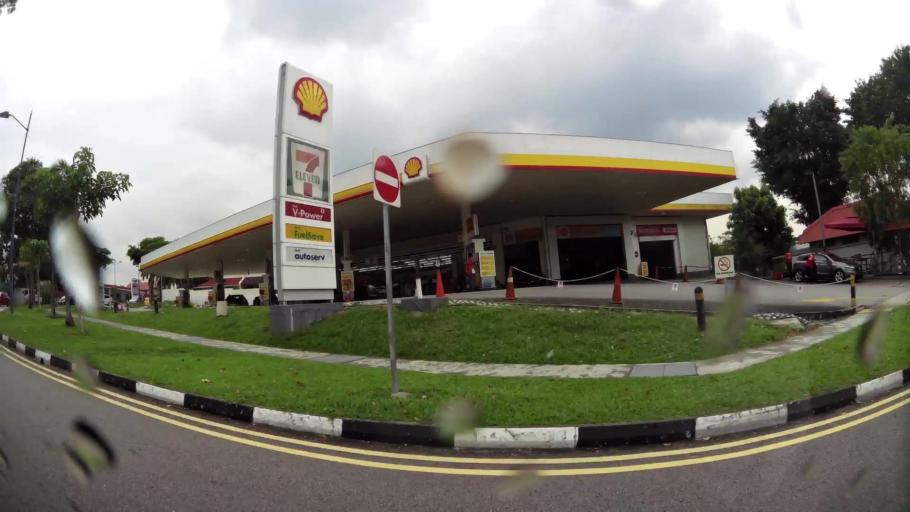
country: SG
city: Singapore
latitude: 1.3636
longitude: 103.8673
